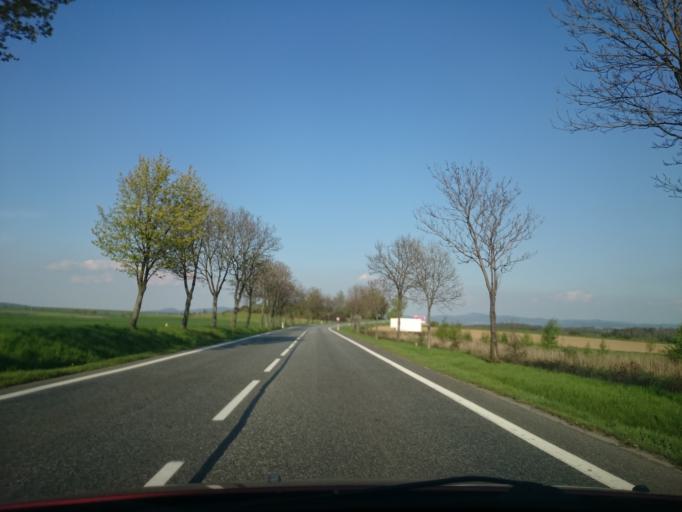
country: PL
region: Lower Silesian Voivodeship
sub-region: Powiat klodzki
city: Polanica-Zdroj
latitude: 50.4261
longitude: 16.5264
